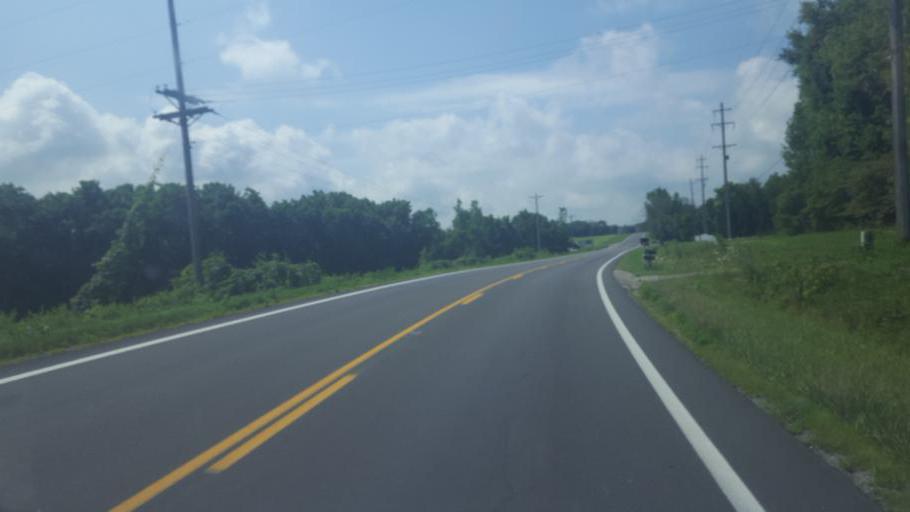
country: US
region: Ohio
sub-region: Fairfield County
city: Baltimore
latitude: 39.8090
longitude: -82.5708
